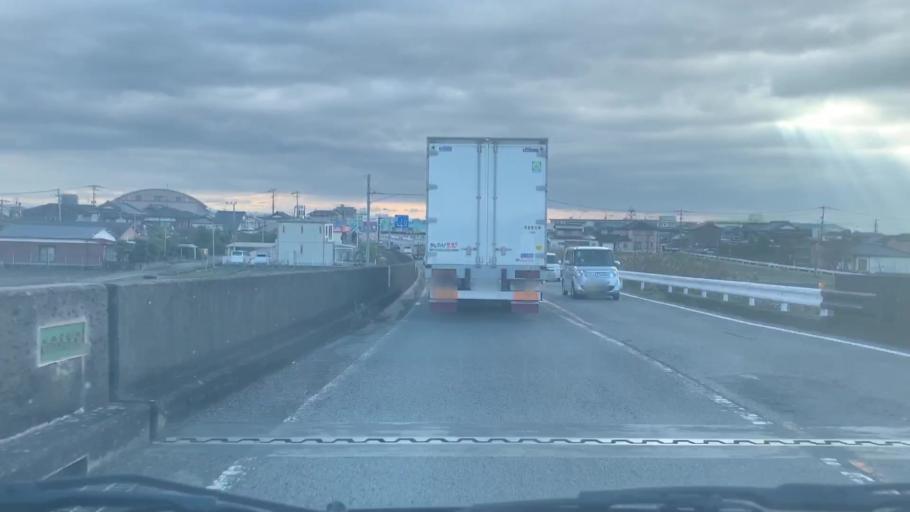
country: JP
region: Saga Prefecture
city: Kashima
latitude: 33.2188
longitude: 130.1548
